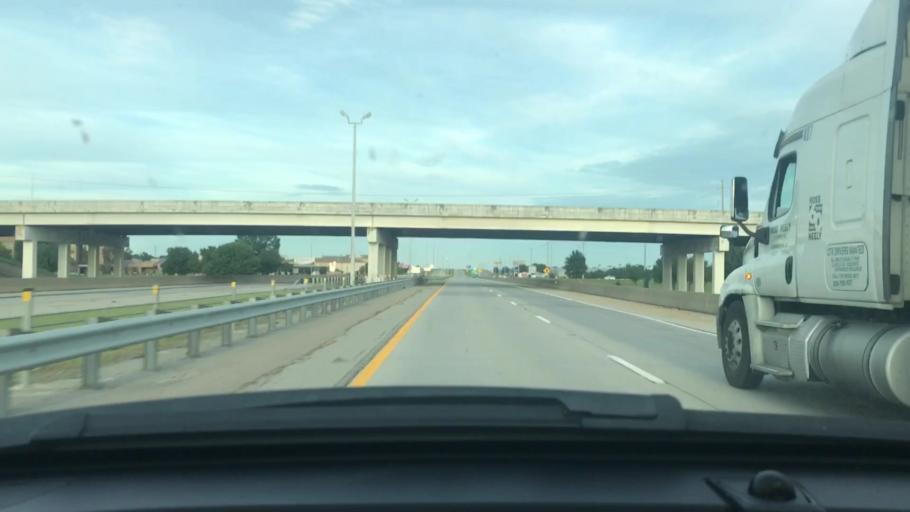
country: US
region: Arkansas
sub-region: Craighead County
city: Jonesboro
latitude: 35.8070
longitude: -90.6702
